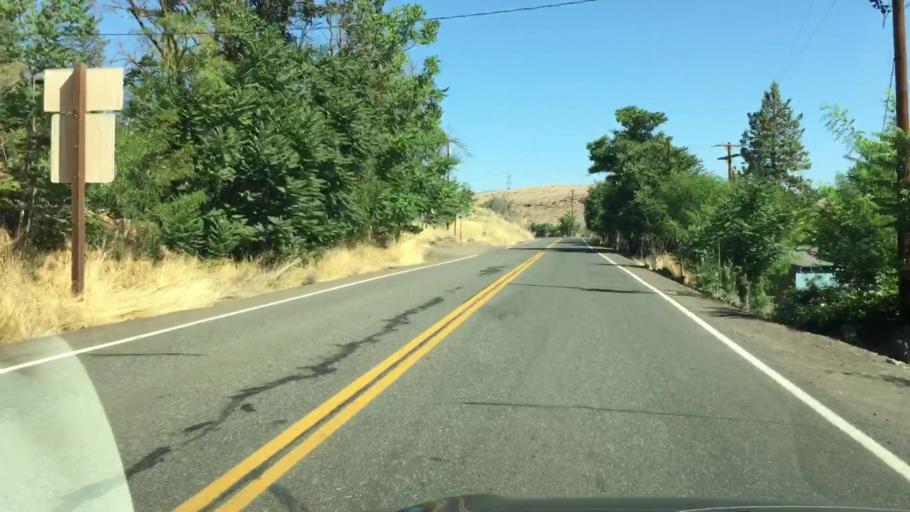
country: US
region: Oregon
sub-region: Wasco County
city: The Dalles
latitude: 45.1749
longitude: -121.0762
